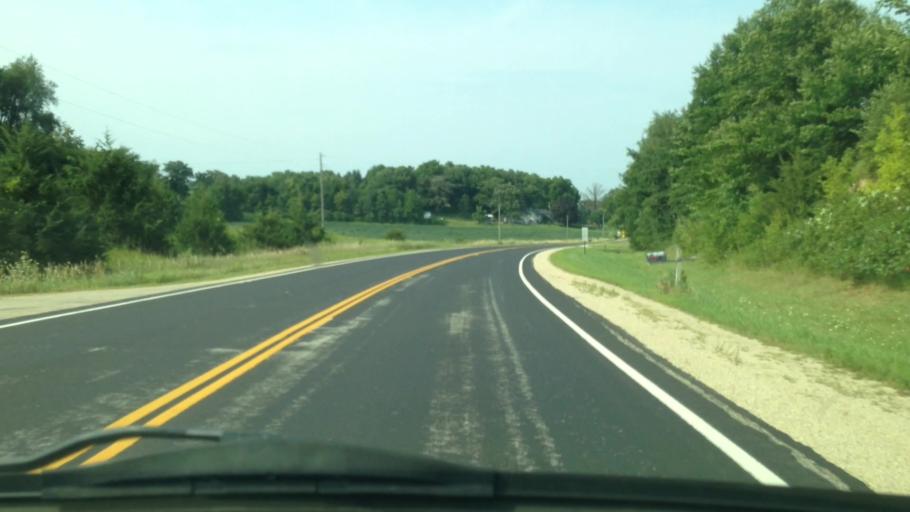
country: US
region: Minnesota
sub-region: Winona County
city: Lewiston
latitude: 43.9656
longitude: -91.9543
